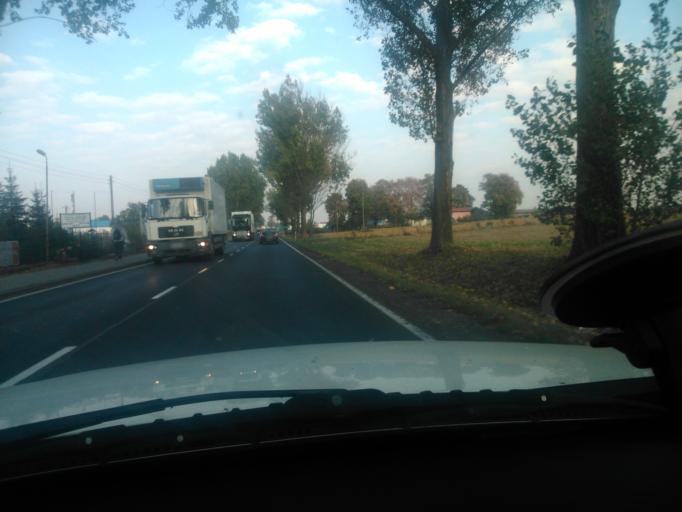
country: PL
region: Kujawsko-Pomorskie
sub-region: Powiat golubsko-dobrzynski
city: Kowalewo Pomorskie
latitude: 53.1596
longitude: 18.9112
